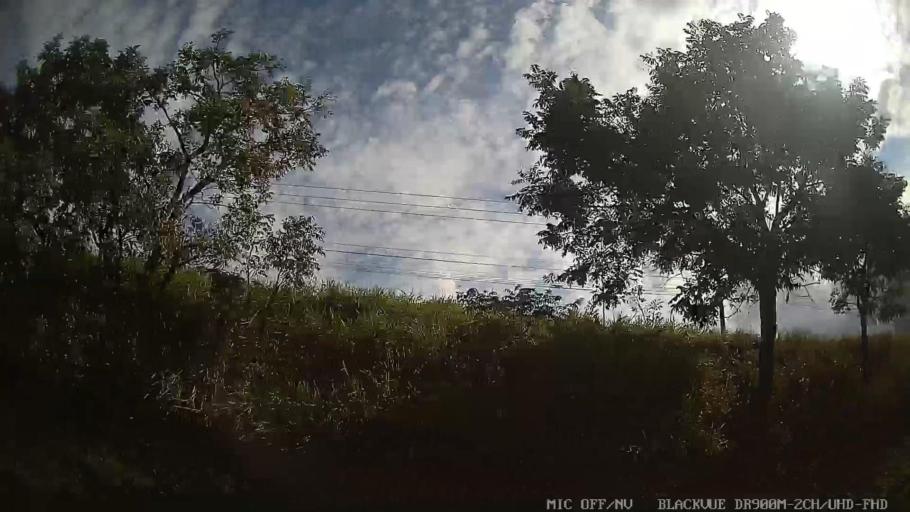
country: BR
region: Sao Paulo
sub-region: Salto
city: Salto
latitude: -23.1472
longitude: -47.2526
